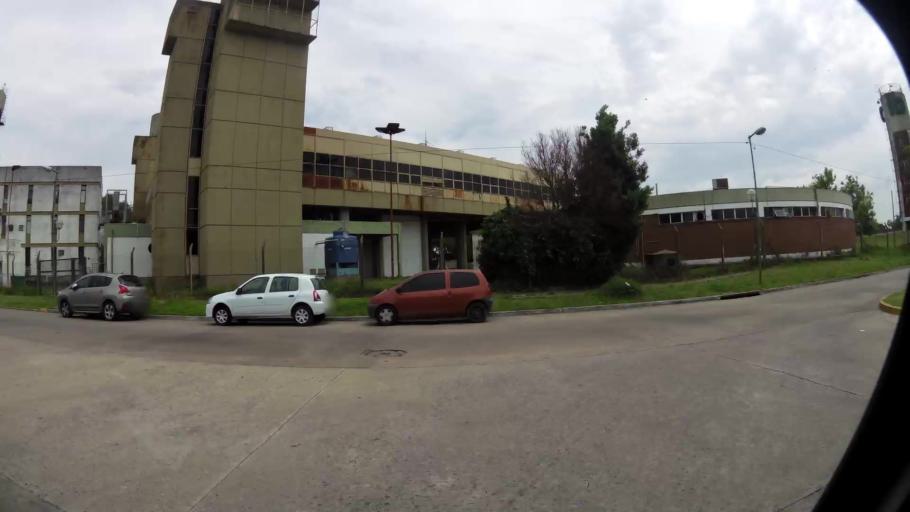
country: AR
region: Buenos Aires
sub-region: Partido de La Plata
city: La Plata
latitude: -34.8983
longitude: -57.9787
